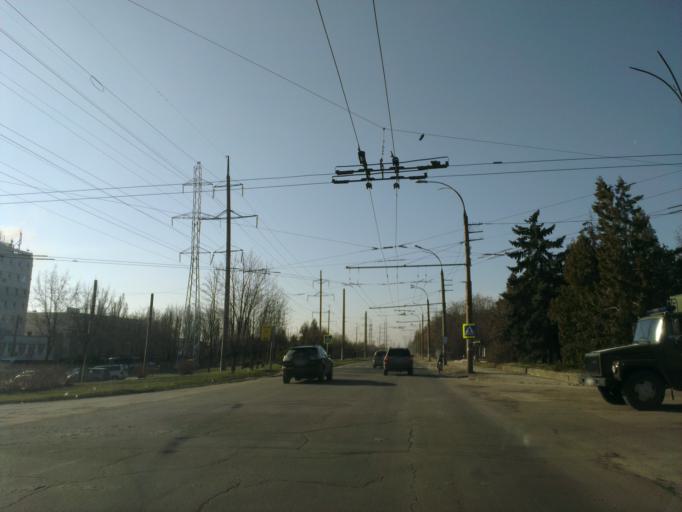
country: MD
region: Chisinau
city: Chisinau
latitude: 47.0256
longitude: 28.8879
